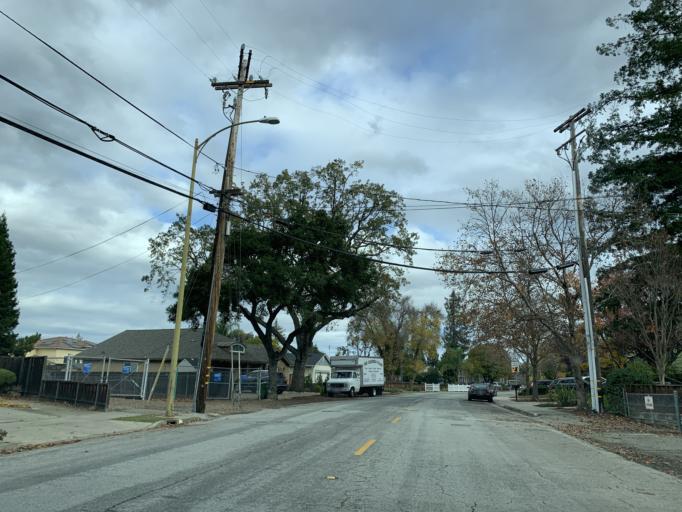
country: US
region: California
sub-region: Santa Clara County
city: Campbell
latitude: 37.2688
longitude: -121.9775
